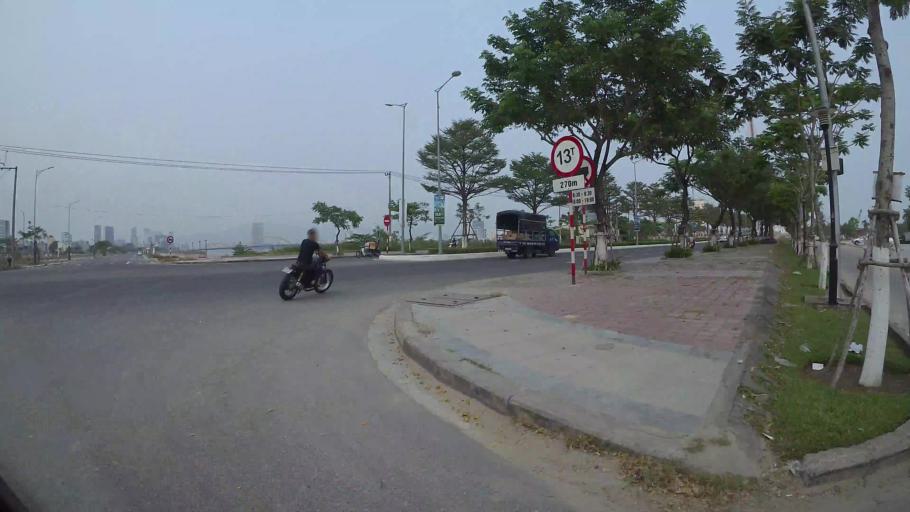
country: VN
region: Da Nang
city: Son Tra
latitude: 16.0495
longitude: 108.2239
